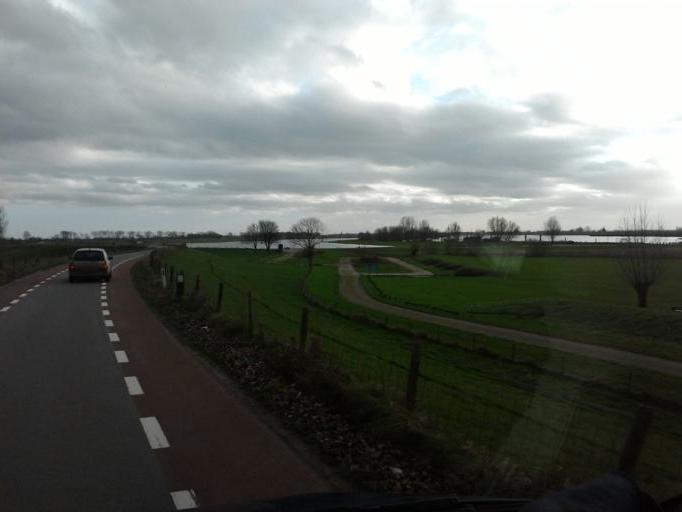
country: NL
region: Utrecht
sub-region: Gemeente Houten
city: Houten
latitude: 51.9955
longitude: 5.1430
